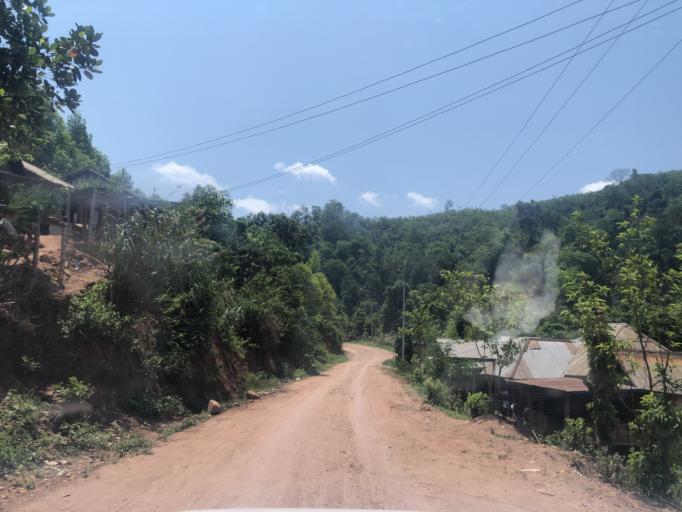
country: LA
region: Phongsali
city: Phongsali
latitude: 21.4263
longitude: 102.0168
